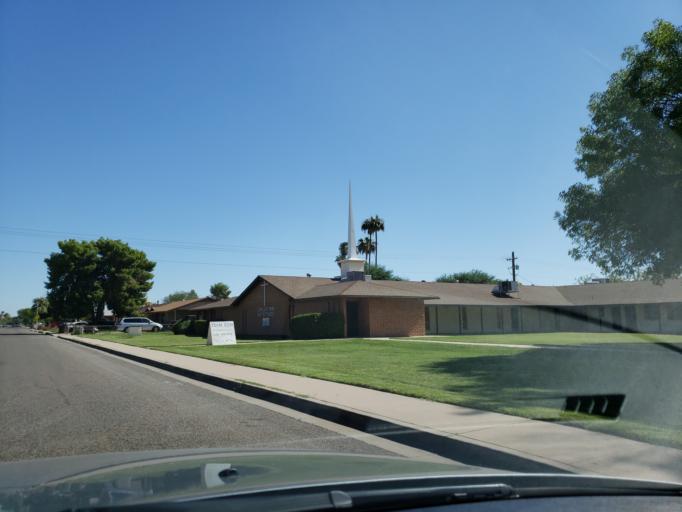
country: US
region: Arizona
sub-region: Maricopa County
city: Tolleson
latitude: 33.4872
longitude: -112.2298
